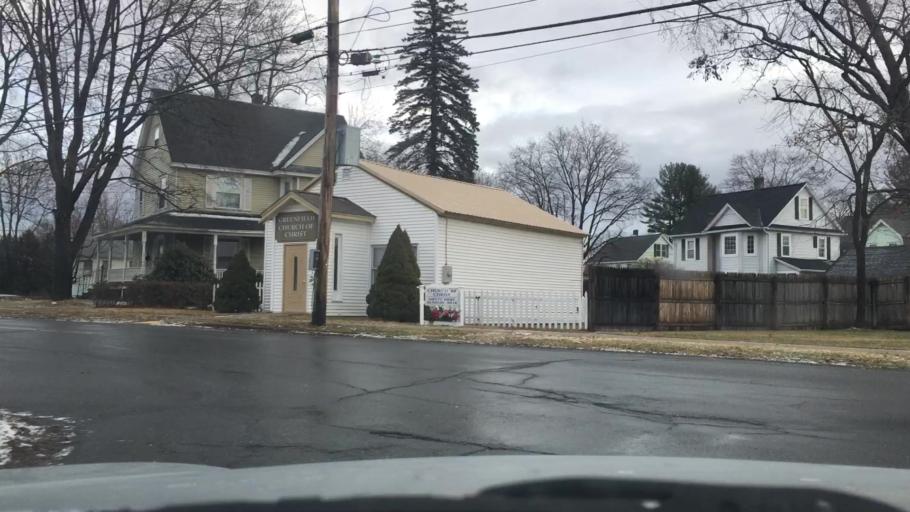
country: US
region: Massachusetts
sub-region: Franklin County
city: Greenfield
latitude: 42.6036
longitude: -72.6112
